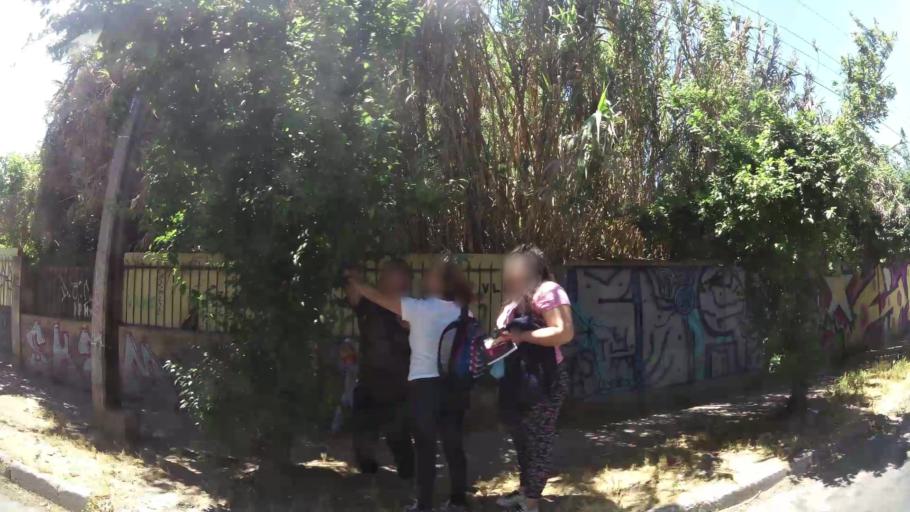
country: CL
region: Santiago Metropolitan
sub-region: Provincia de Santiago
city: La Pintana
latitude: -33.5739
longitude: -70.6628
